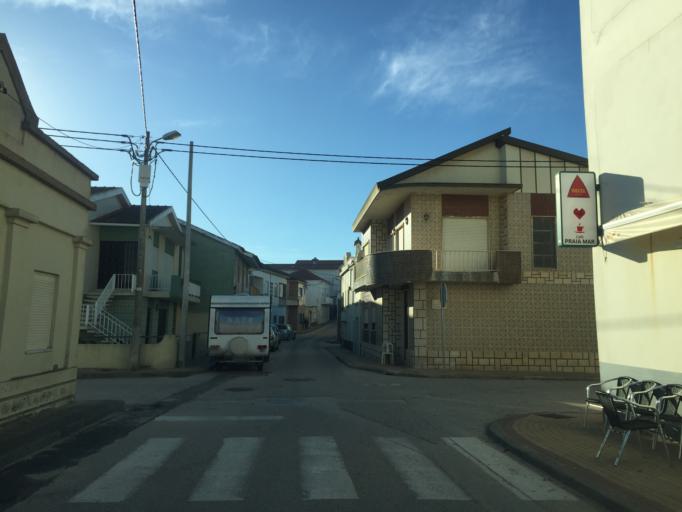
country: PT
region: Coimbra
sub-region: Figueira da Foz
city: Lavos
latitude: 40.0914
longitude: -8.8738
